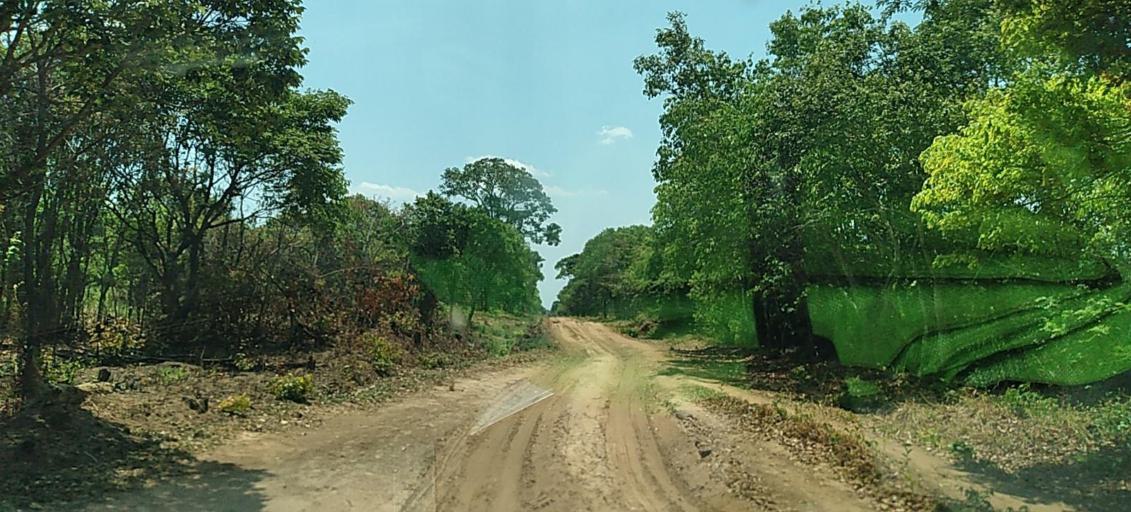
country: CD
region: Katanga
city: Kolwezi
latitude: -11.3879
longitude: 25.2207
